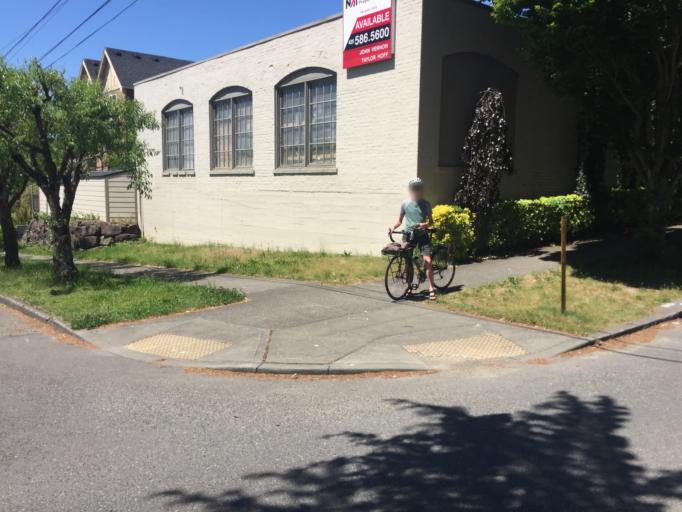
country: US
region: Washington
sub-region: King County
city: Seattle
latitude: 47.5983
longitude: -122.3090
